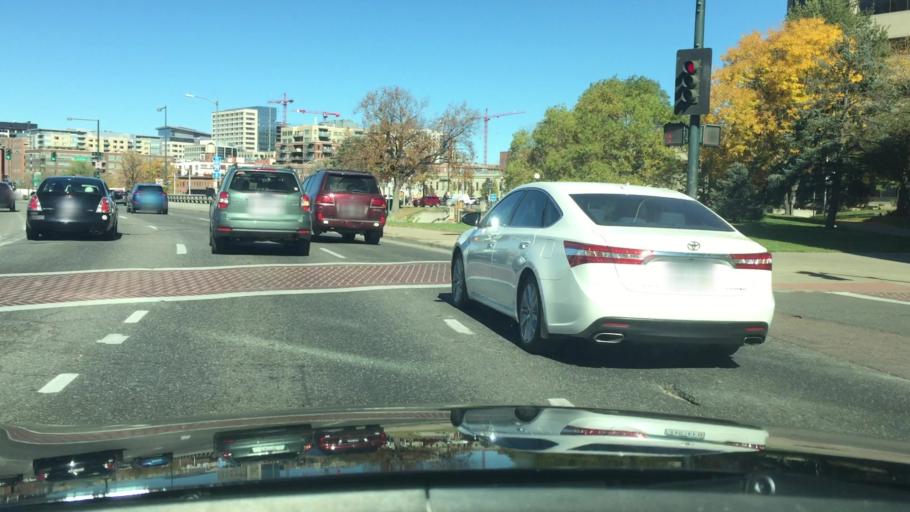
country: US
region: Colorado
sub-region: Denver County
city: Denver
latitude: 39.7457
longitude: -105.0002
